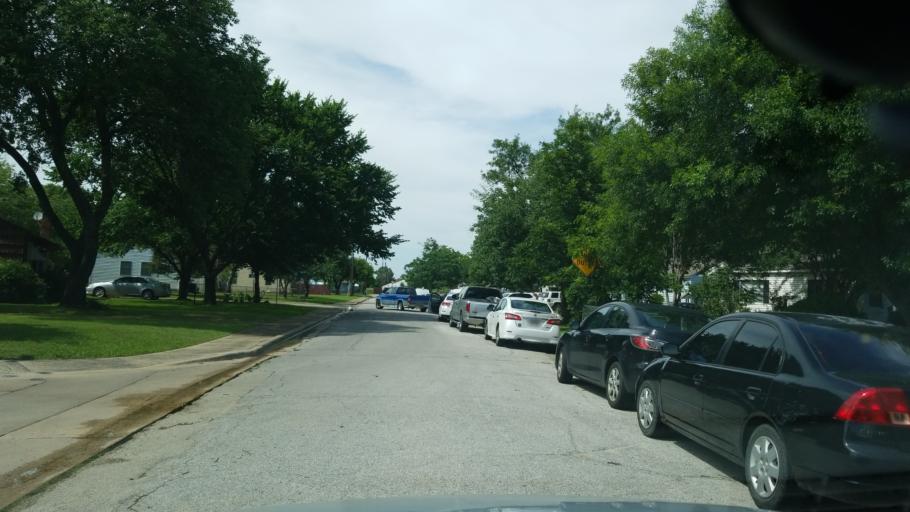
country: US
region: Texas
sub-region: Dallas County
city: Irving
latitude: 32.8312
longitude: -96.9416
